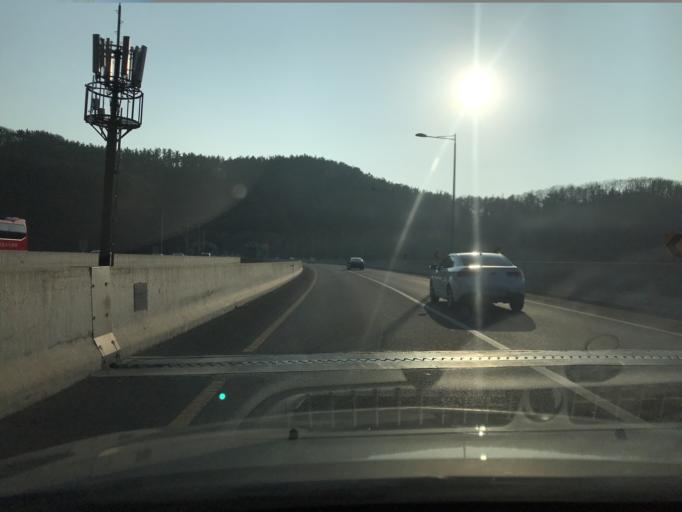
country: KR
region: Daegu
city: Hwawon
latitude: 35.7985
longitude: 128.5119
